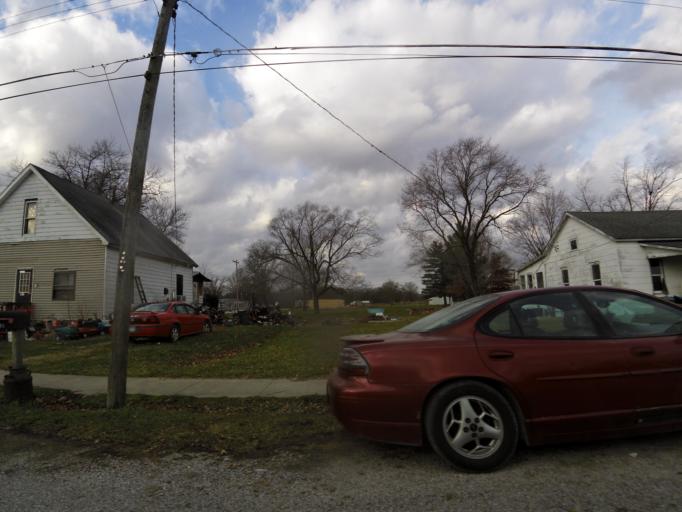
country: US
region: Illinois
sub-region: Fayette County
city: Ramsey
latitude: 39.1384
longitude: -89.1098
